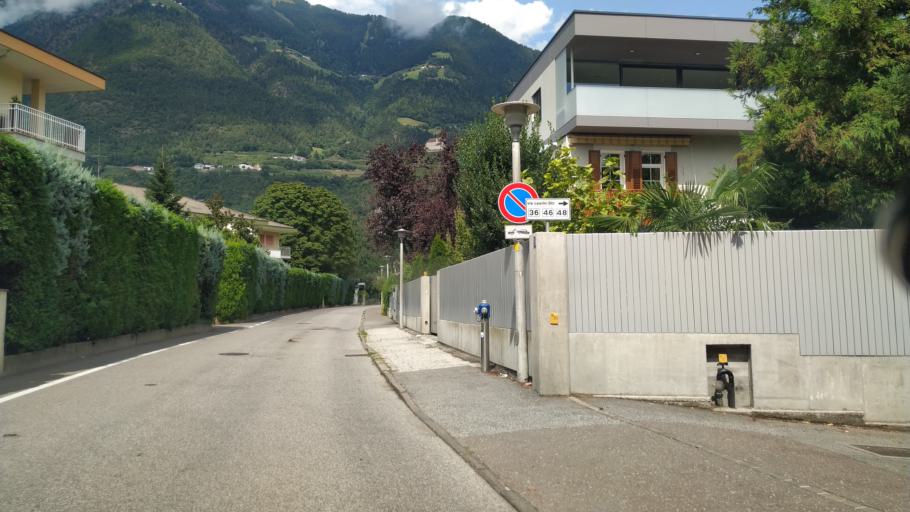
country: IT
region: Trentino-Alto Adige
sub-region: Bolzano
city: Tirolo
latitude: 46.6802
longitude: 11.1475
